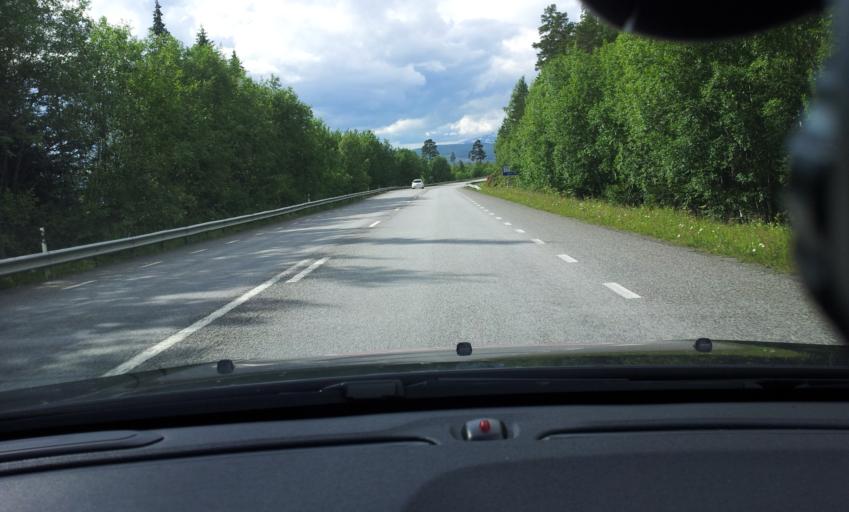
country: SE
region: Jaemtland
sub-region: Are Kommun
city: Jarpen
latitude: 63.3220
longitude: 13.5484
